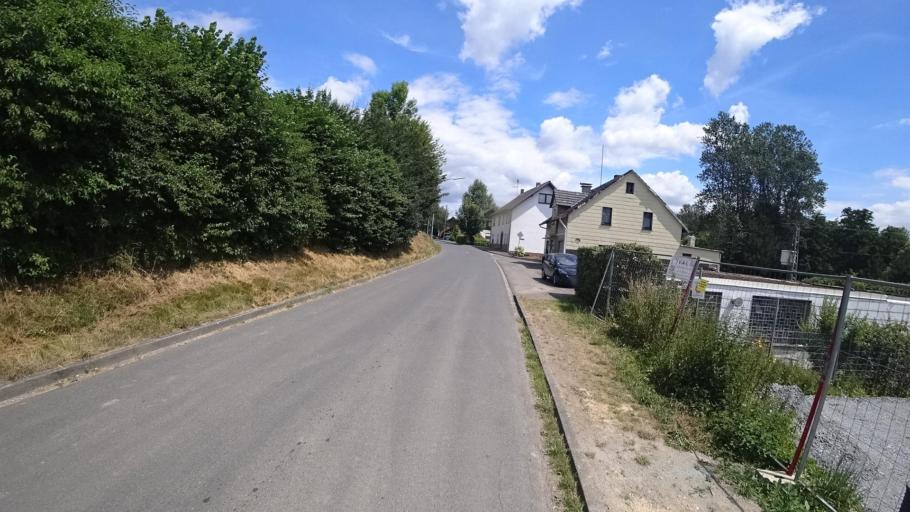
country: DE
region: Rheinland-Pfalz
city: Forstmehren
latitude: 50.7000
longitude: 7.5278
